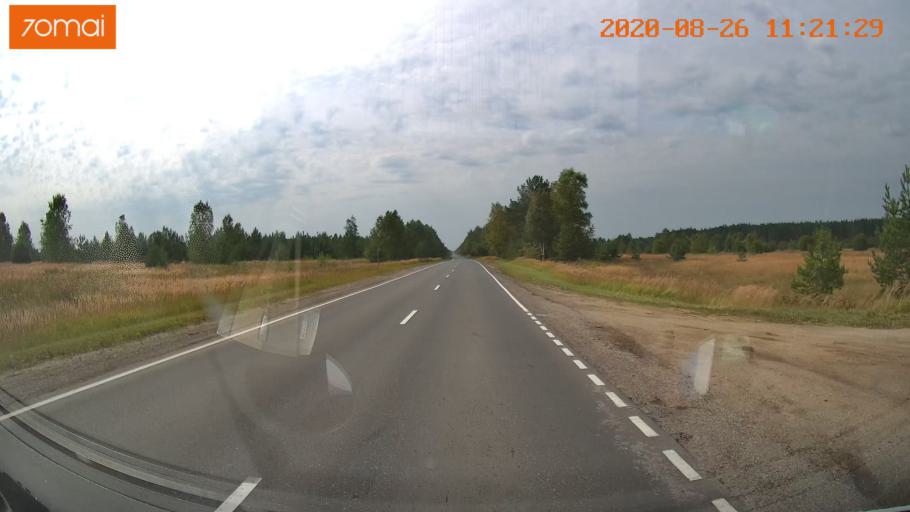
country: RU
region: Rjazan
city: Shilovo
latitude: 54.3755
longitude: 41.0438
